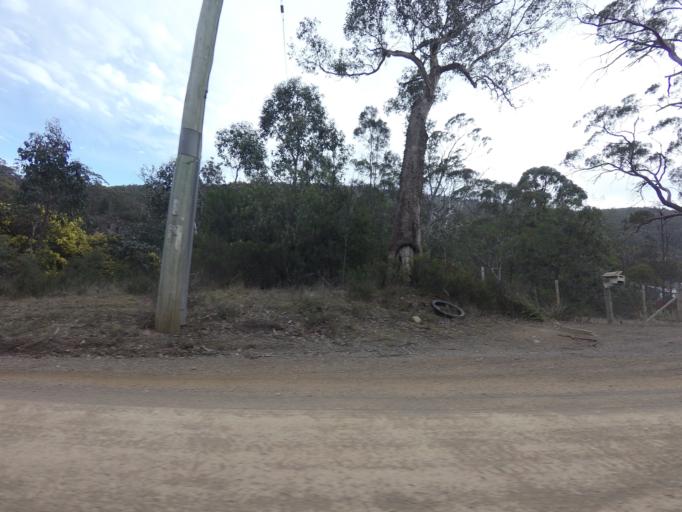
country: AU
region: Tasmania
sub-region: Huon Valley
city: Huonville
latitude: -43.0624
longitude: 147.0935
